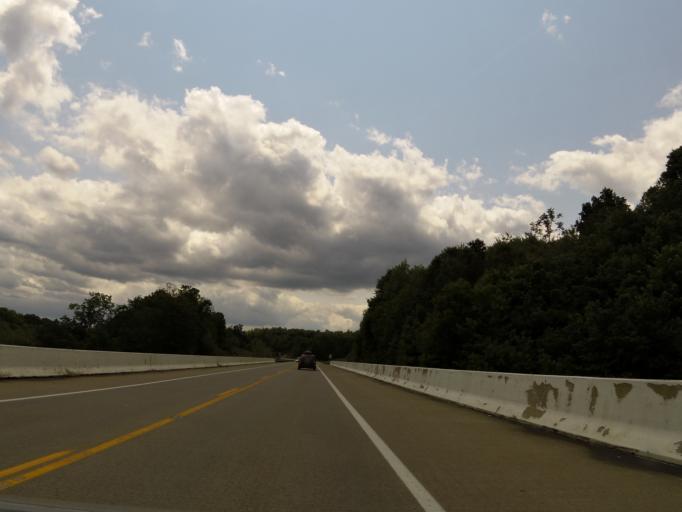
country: US
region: Ohio
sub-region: Athens County
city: Athens
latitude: 39.2194
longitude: -82.0651
